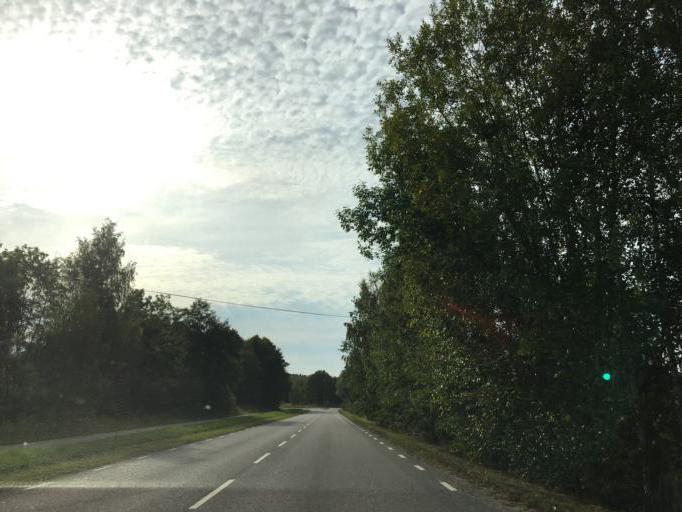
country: SE
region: Soedermanland
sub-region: Eskilstuna Kommun
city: Torshalla
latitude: 59.4369
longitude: 16.4648
